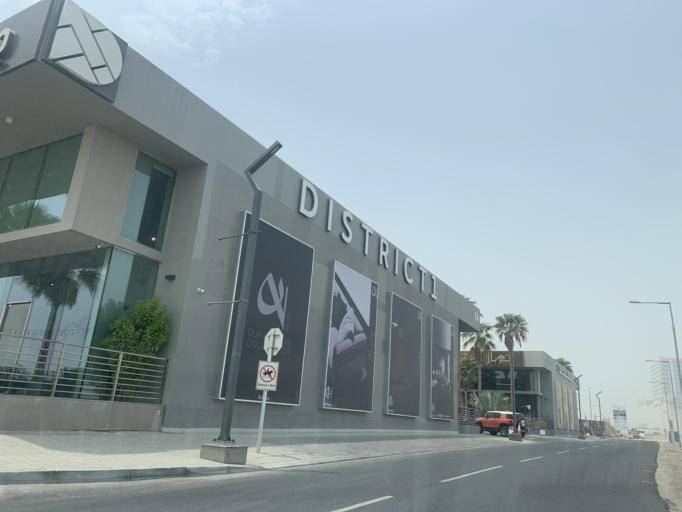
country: BH
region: Central Governorate
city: Madinat Hamad
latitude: 26.1716
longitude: 50.4834
